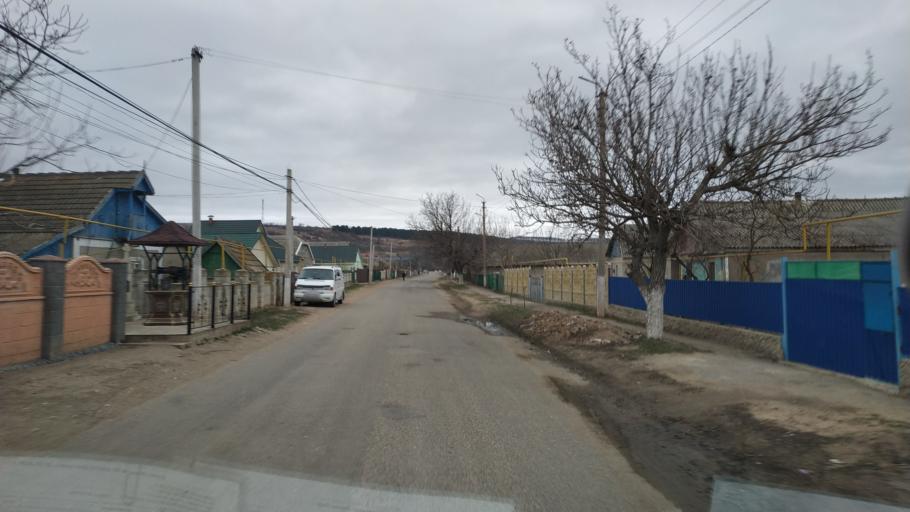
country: MD
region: Causeni
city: Causeni
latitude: 46.6667
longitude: 29.4834
